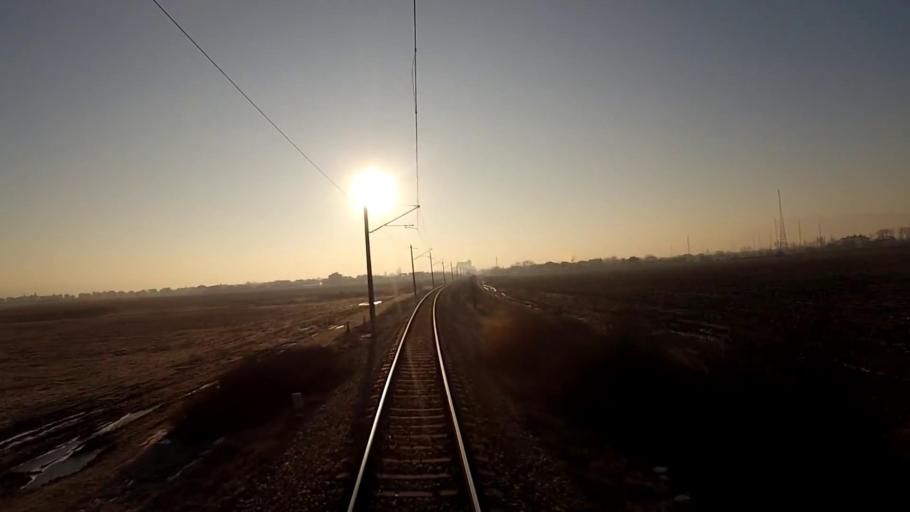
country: BG
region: Sofiya
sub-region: Obshtina Kostinbrod
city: Kostinbrod
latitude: 42.8076
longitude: 23.1989
